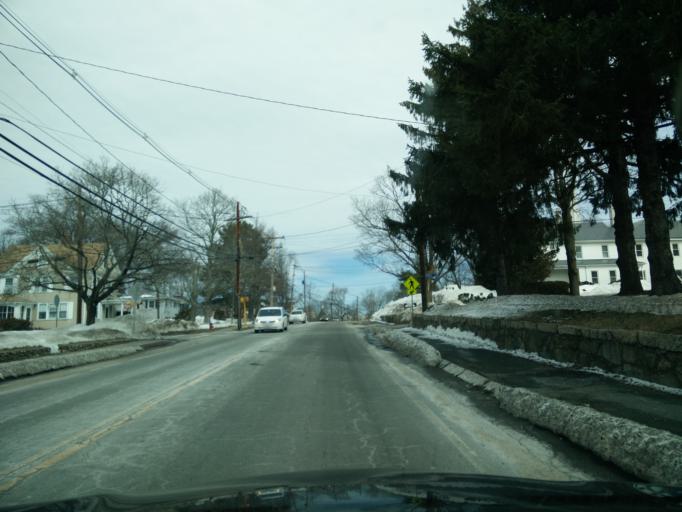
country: US
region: Massachusetts
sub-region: Norfolk County
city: Walpole
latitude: 42.1605
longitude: -71.2400
